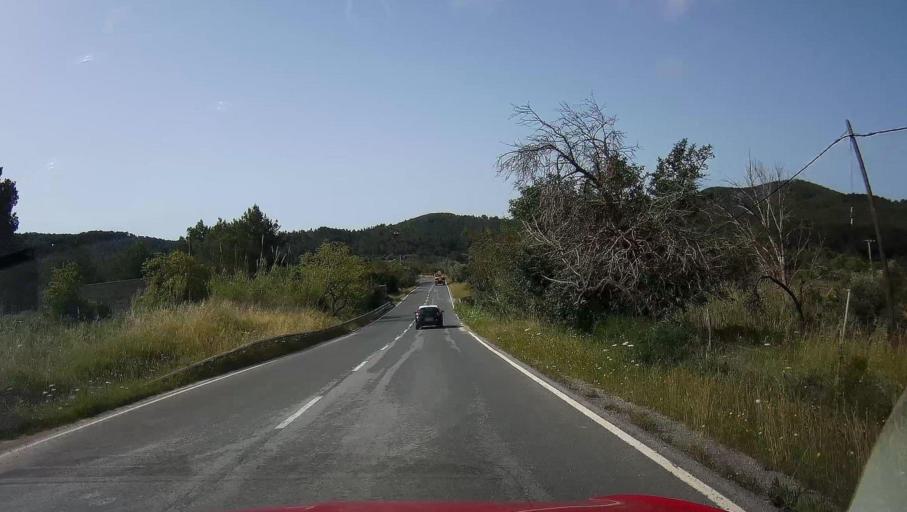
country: ES
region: Balearic Islands
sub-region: Illes Balears
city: Sant Joan de Labritja
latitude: 39.0896
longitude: 1.5025
